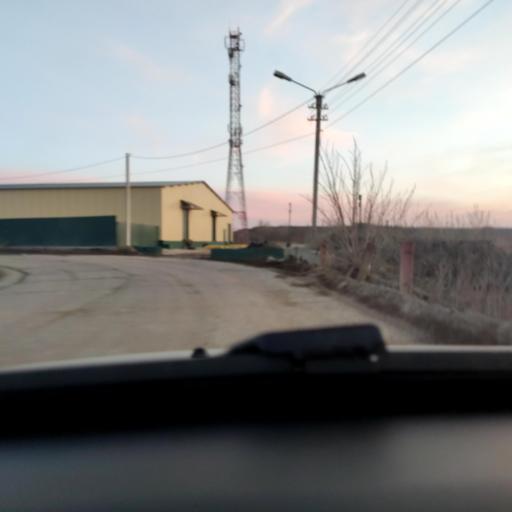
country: RU
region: Voronezj
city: Podgornoye
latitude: 51.7066
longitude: 39.1308
